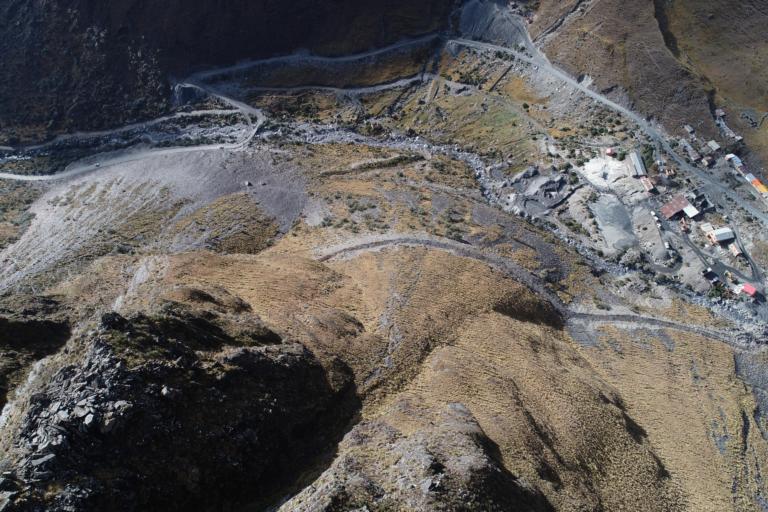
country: BO
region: La Paz
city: Sorata
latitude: -15.6612
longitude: -68.5407
